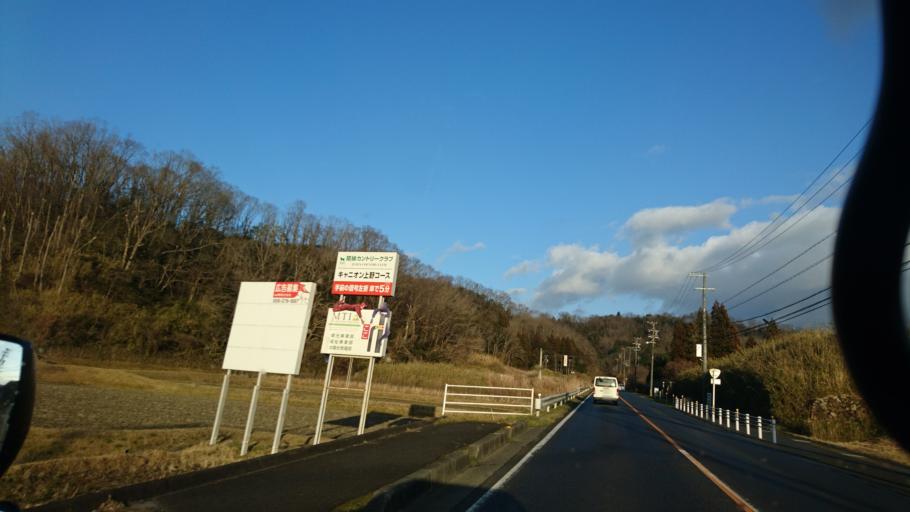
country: JP
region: Mie
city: Ueno-ebisumachi
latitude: 34.7596
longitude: 136.0892
